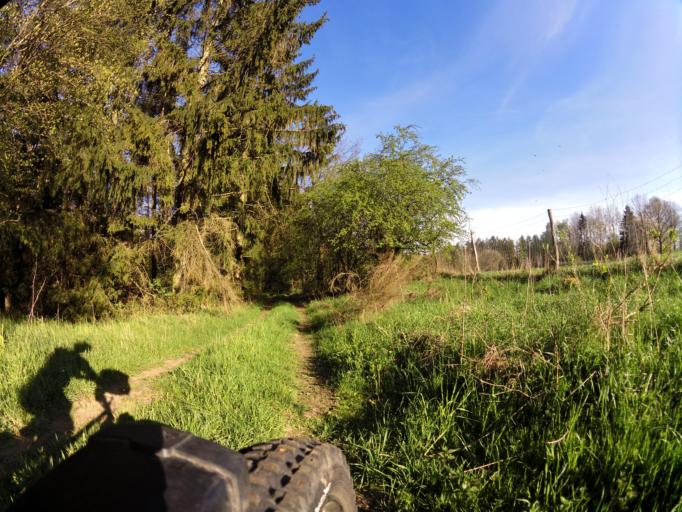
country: PL
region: West Pomeranian Voivodeship
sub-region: Powiat lobeski
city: Lobez
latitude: 53.7492
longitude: 15.6106
